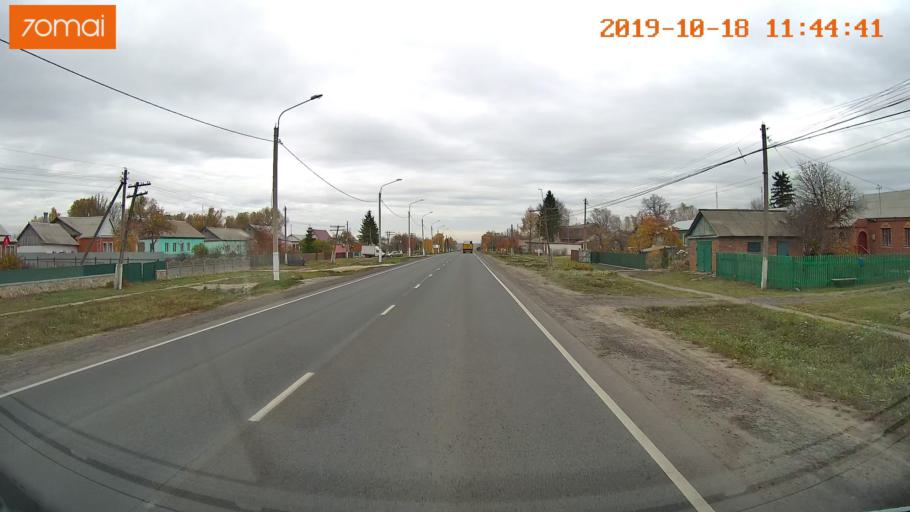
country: RU
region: Rjazan
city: Oktyabr'skiy
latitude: 54.2043
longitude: 38.9610
